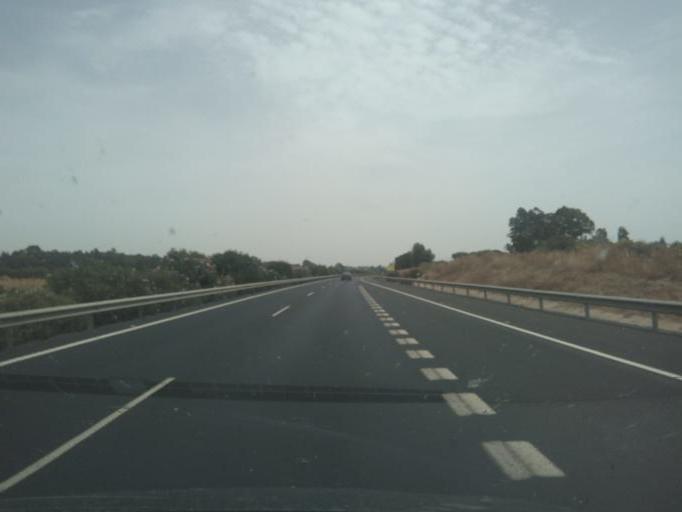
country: ES
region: Andalusia
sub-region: Provincia de Huelva
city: Villarrasa
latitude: 37.3535
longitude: -6.5923
